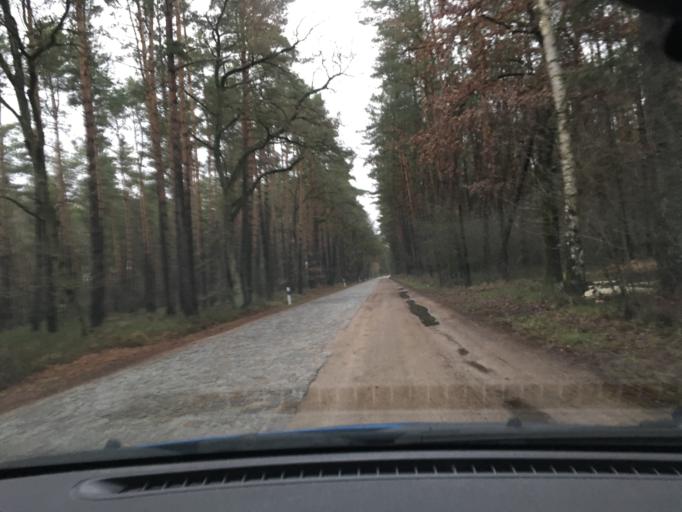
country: DE
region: Schleswig-Holstein
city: Brothen
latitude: 53.4398
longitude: 10.6997
